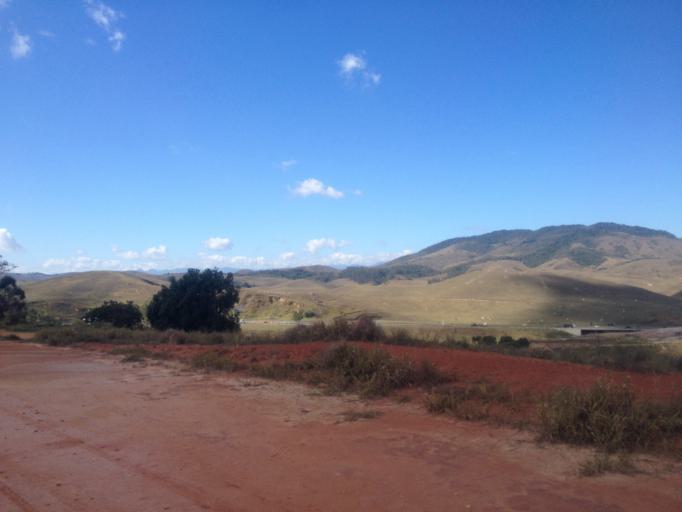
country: BR
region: Rio de Janeiro
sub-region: Porto Real
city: Porto Real
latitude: -22.4446
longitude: -44.3246
